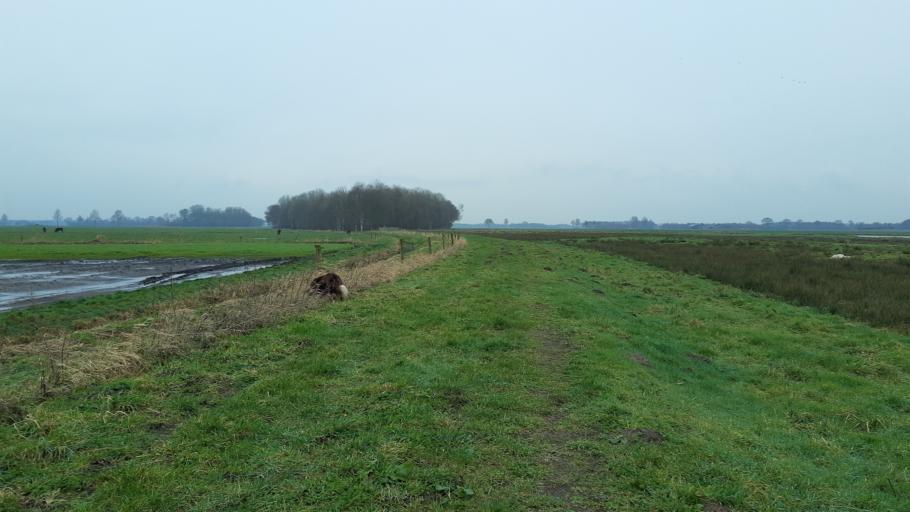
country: NL
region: Groningen
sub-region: Gemeente Veendam
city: Veendam
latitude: 53.0404
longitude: 6.8037
